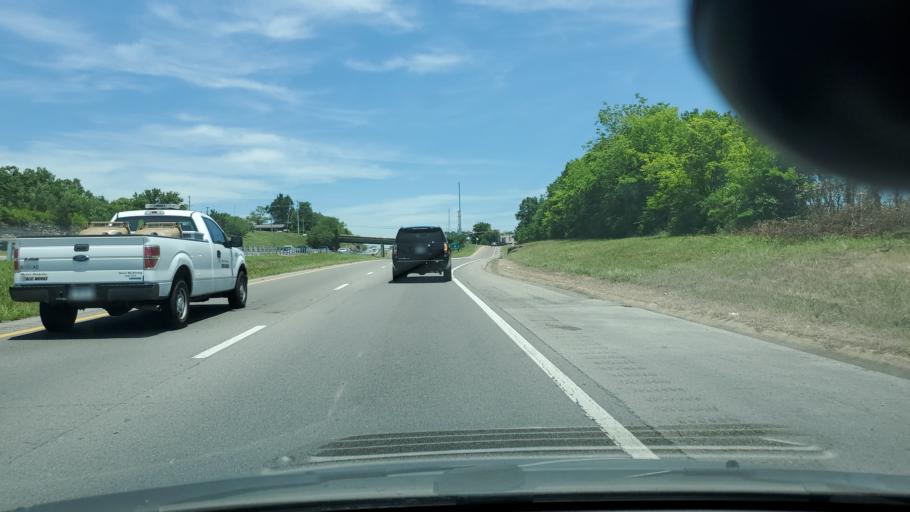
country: US
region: Tennessee
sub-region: Davidson County
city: Nashville
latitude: 36.2021
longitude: -86.7508
